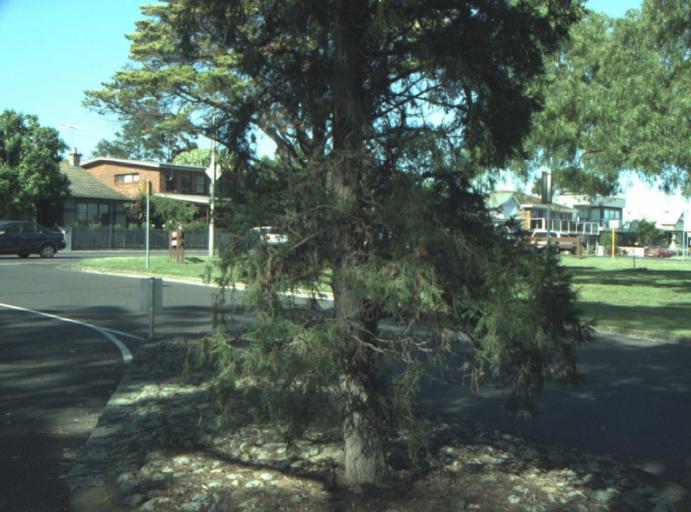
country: AU
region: Victoria
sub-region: Greater Geelong
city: Geelong West
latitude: -38.1277
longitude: 144.3561
